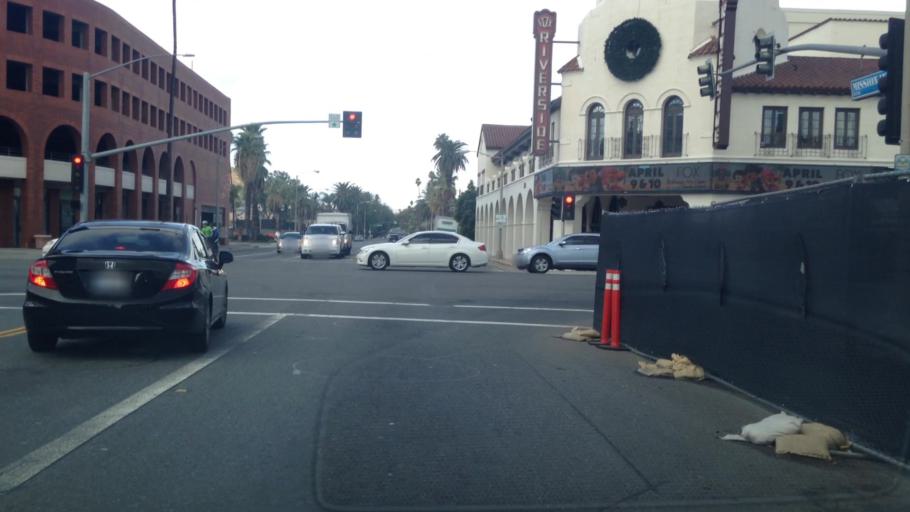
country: US
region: California
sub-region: Riverside County
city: Rubidoux
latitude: 33.9834
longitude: -117.3747
